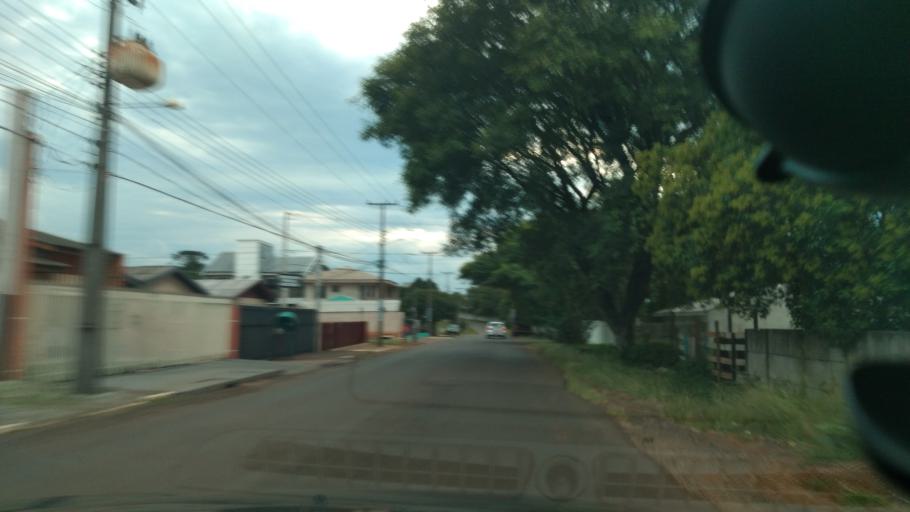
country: BR
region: Parana
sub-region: Guarapuava
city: Guarapuava
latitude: -25.3891
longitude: -51.4839
